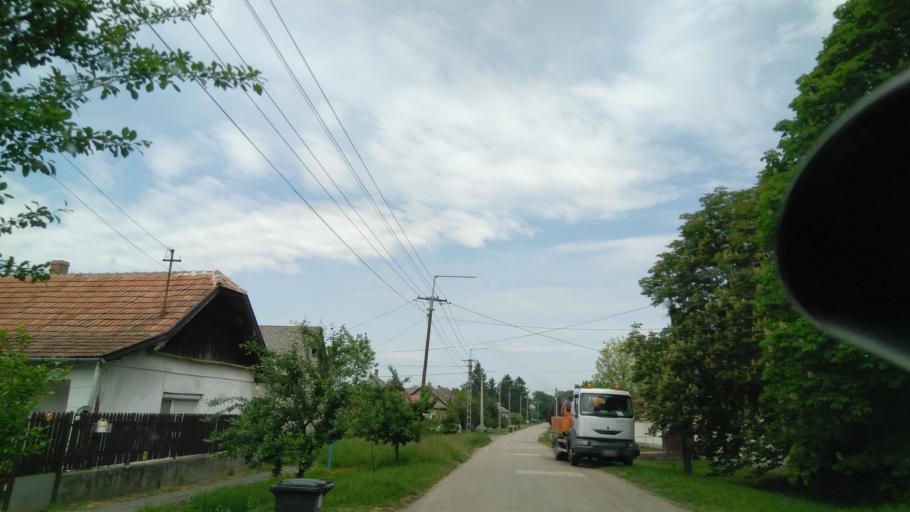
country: HU
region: Bekes
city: Fuzesgyarmat
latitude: 47.1034
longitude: 21.2055
